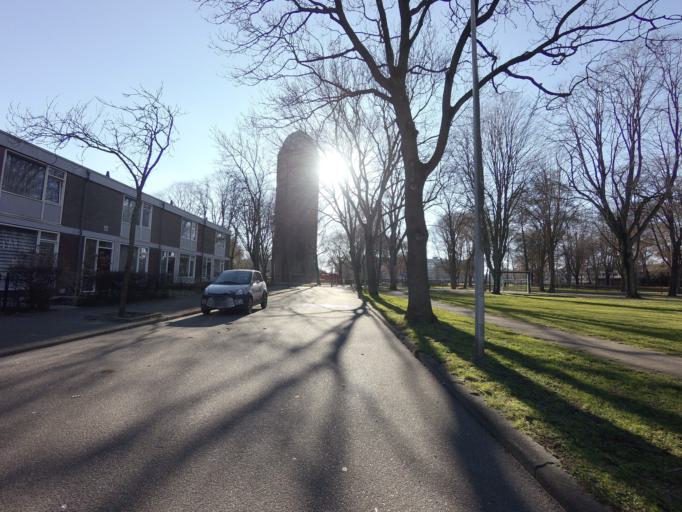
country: NL
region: Utrecht
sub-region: Gemeente Utrecht
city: Utrecht
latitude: 52.1174
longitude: 5.1213
